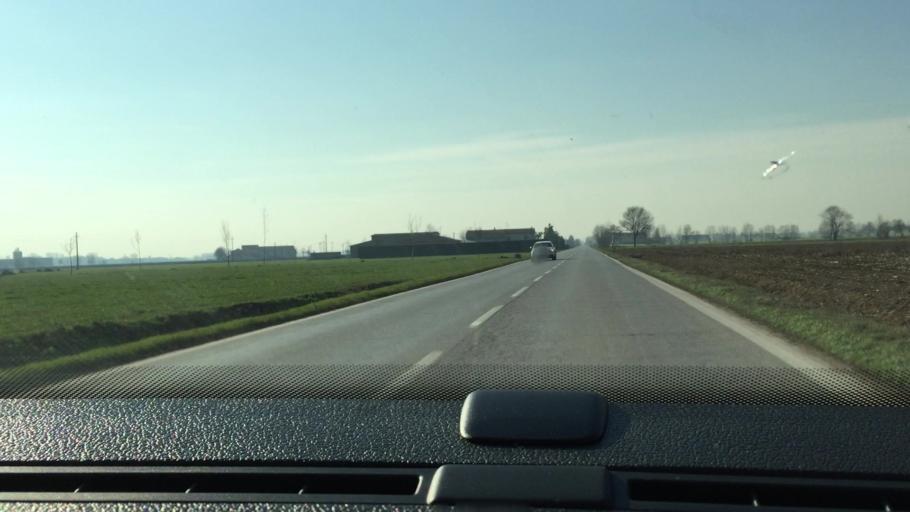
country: IT
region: Lombardy
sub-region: Provincia di Mantova
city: Goito
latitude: 45.2332
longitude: 10.6363
